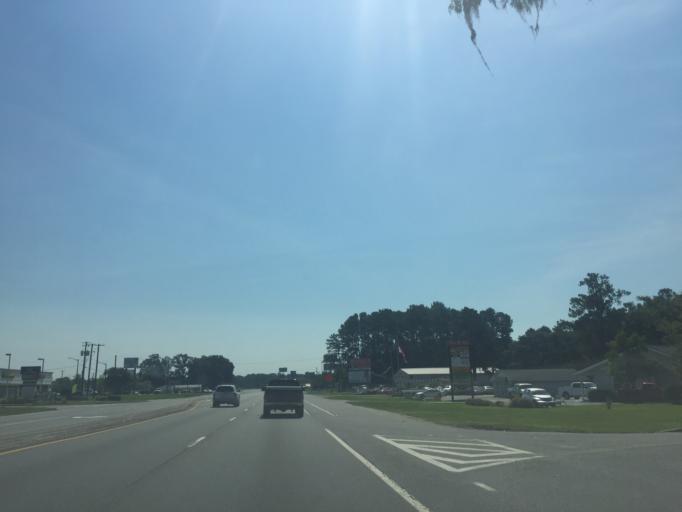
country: US
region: Georgia
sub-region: Chatham County
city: Georgetown
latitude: 31.9977
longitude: -81.2563
